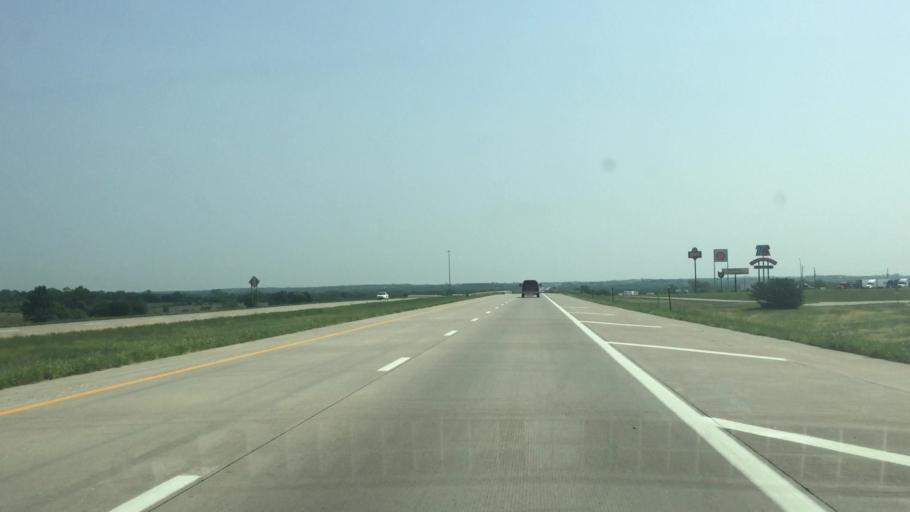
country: US
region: Kansas
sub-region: Osage County
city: Lyndon
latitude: 38.4282
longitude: -95.7313
